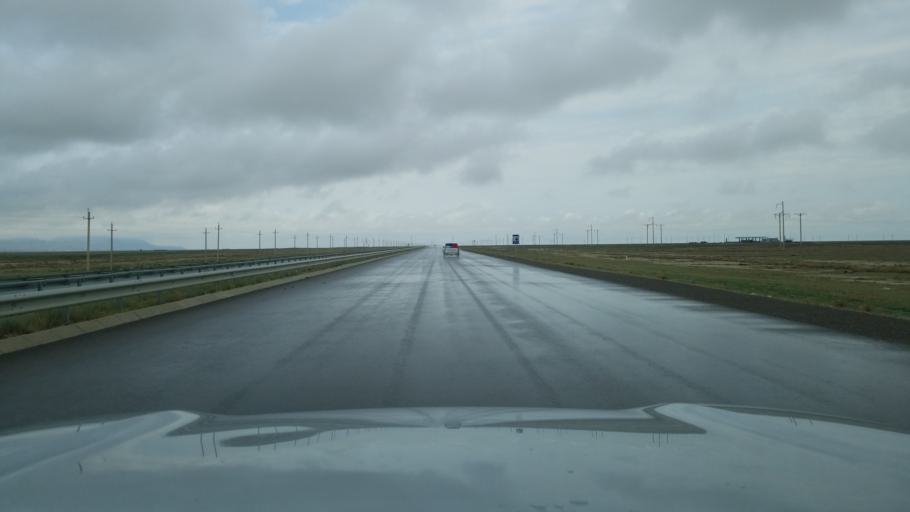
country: TM
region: Balkan
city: Gazanjyk
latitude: 39.1436
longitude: 55.8675
